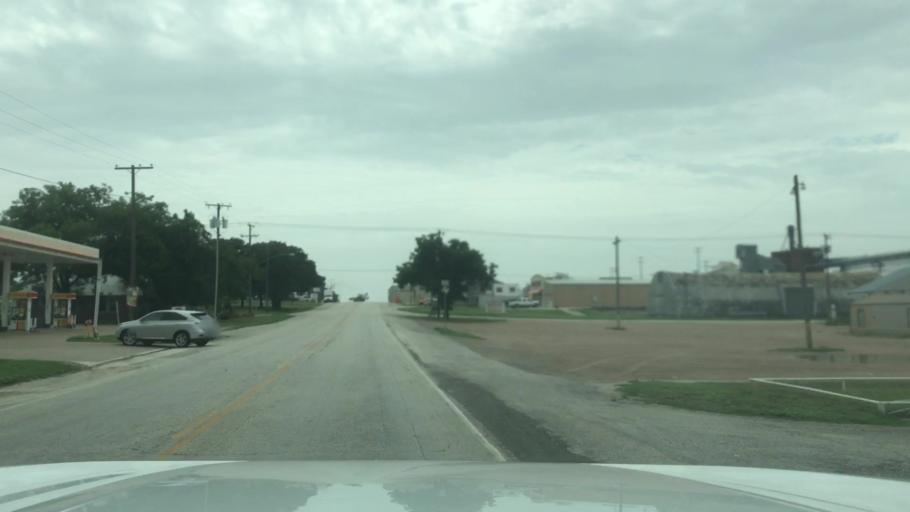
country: US
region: Texas
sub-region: Eastland County
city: Gorman
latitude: 32.2119
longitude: -98.6684
